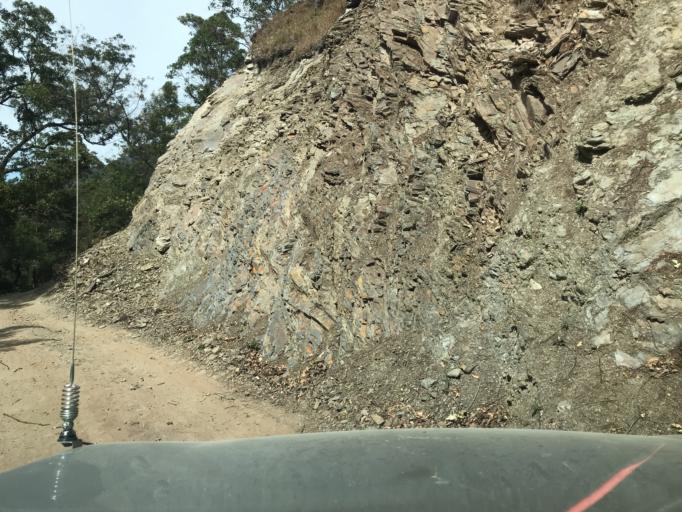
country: TL
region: Ainaro
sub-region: Ainaro
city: Ainaro
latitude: -8.8808
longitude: 125.5296
